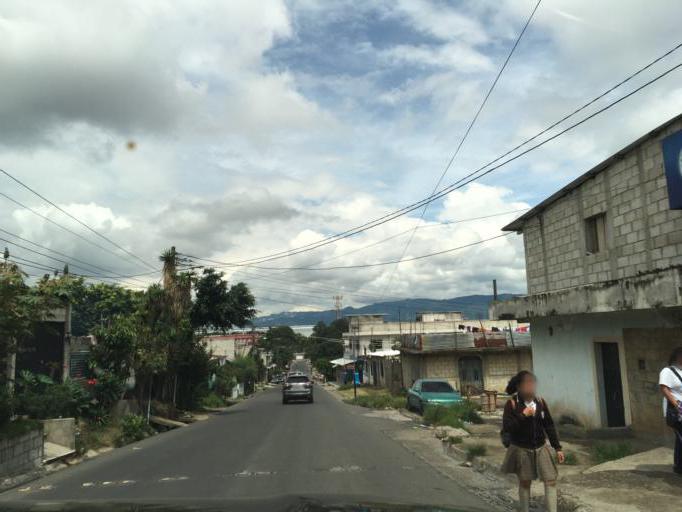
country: GT
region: Guatemala
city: Villa Nueva
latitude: 14.5058
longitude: -90.5881
